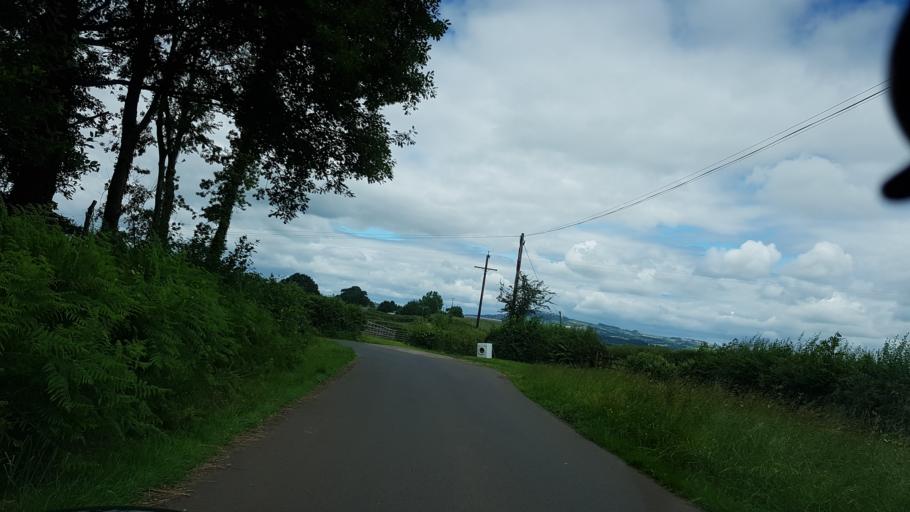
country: GB
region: Wales
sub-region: Monmouthshire
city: Llanarth
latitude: 51.7997
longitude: -2.8289
